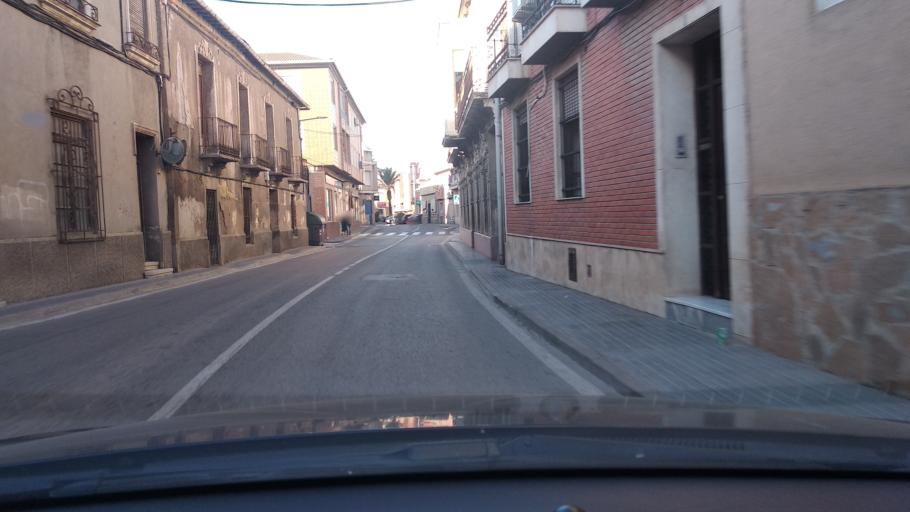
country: ES
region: Murcia
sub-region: Murcia
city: Murcia
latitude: 37.9448
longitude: -1.1125
